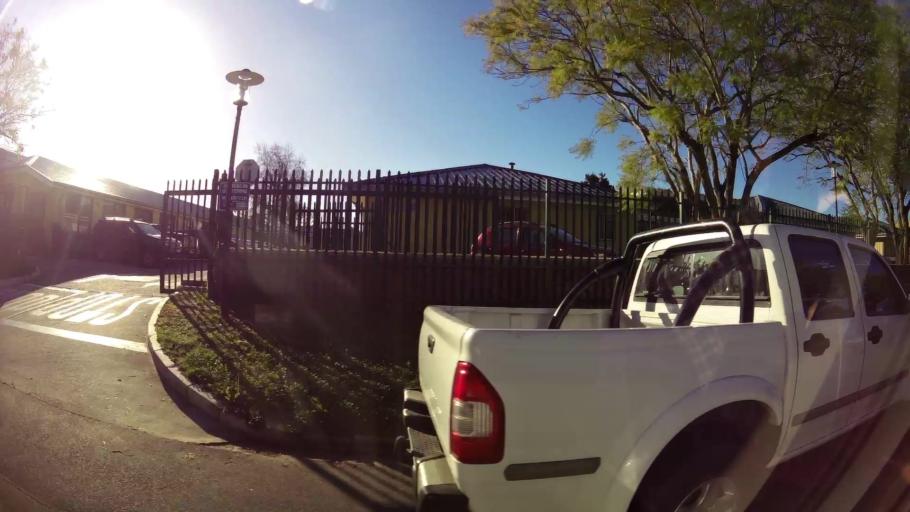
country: ZA
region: Western Cape
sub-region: Eden District Municipality
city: George
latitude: -33.9483
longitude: 22.4511
